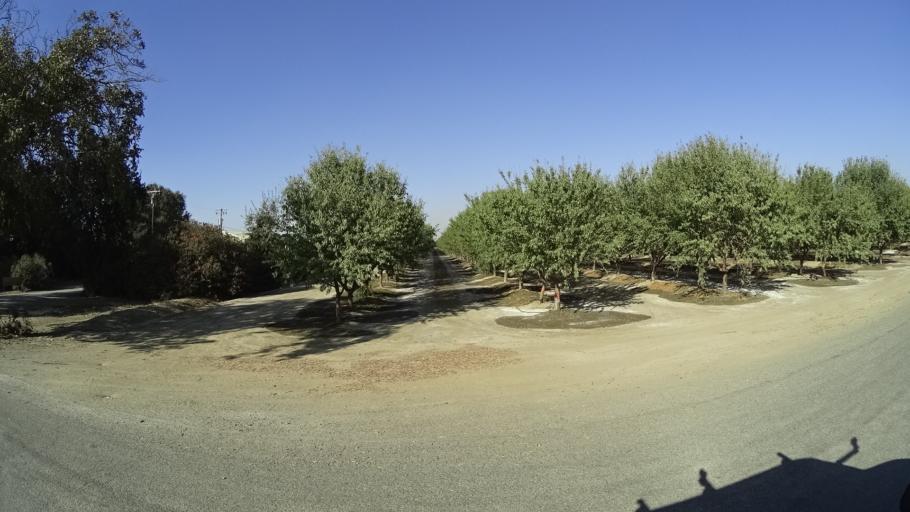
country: US
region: California
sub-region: Yolo County
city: Woodland
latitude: 38.7495
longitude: -121.7794
